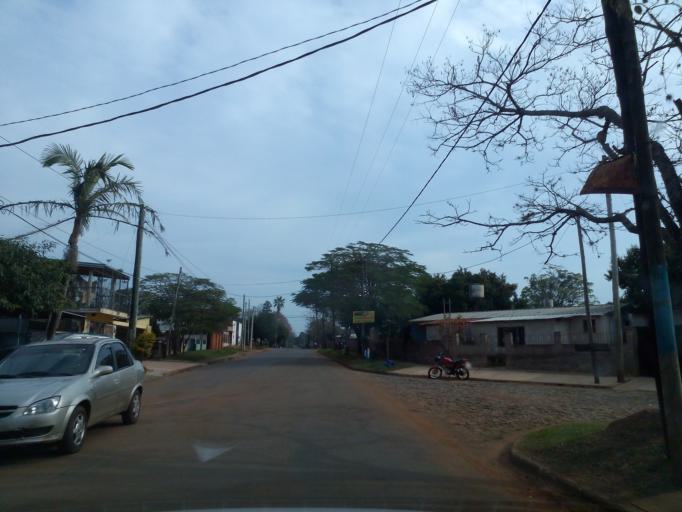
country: AR
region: Misiones
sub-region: Departamento de Capital
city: Posadas
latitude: -27.4254
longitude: -55.8851
